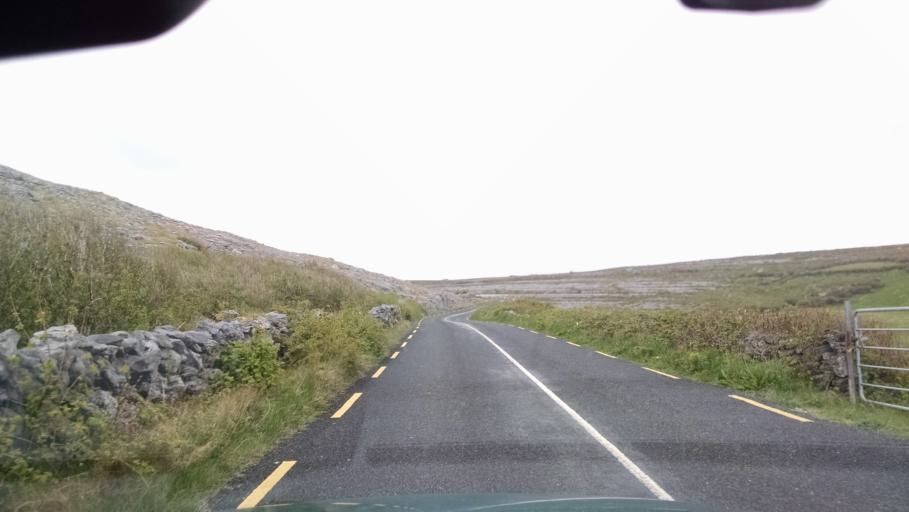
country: IE
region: Connaught
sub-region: County Galway
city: Bearna
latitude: 53.0799
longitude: -9.1647
